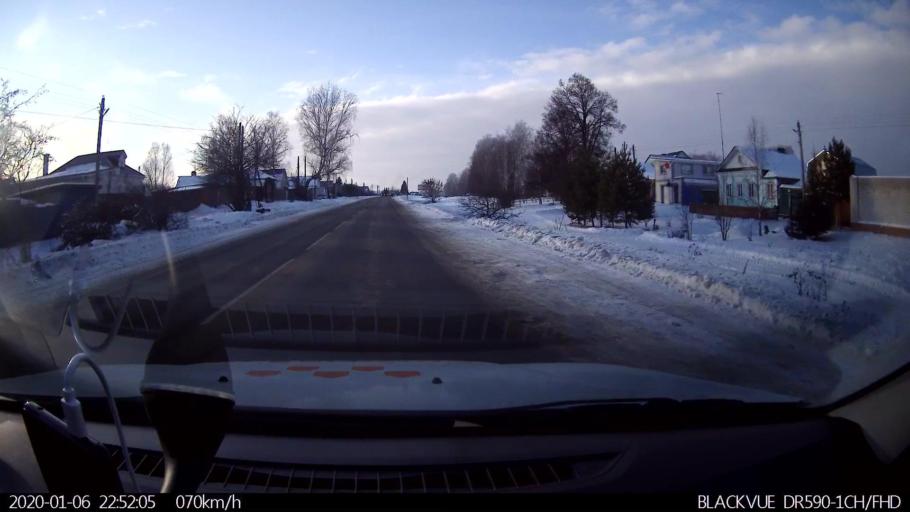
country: RU
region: Nizjnij Novgorod
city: Bogorodsk
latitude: 56.1283
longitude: 43.5883
